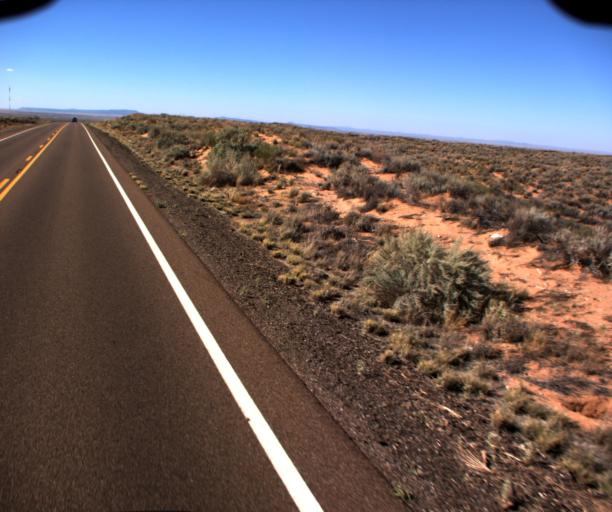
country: US
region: Arizona
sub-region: Navajo County
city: Winslow
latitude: 35.0391
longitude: -110.6116
